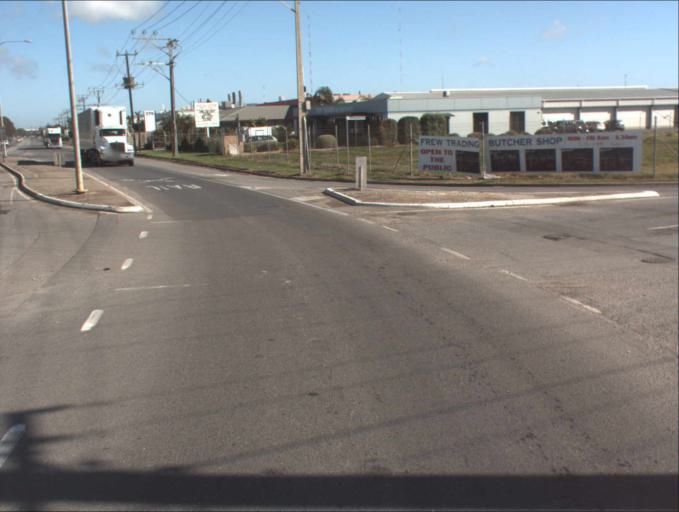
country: AU
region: South Australia
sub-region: Port Adelaide Enfield
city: Blair Athol
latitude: -34.8397
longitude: 138.5819
